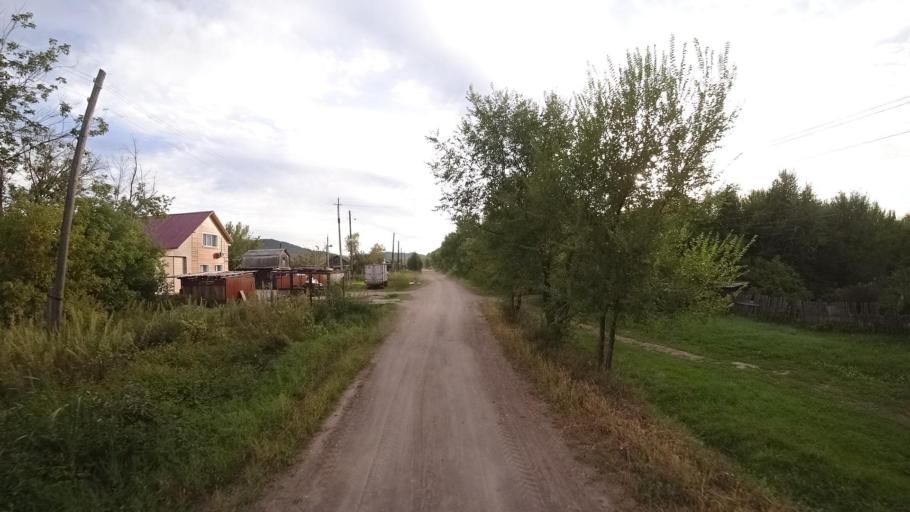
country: RU
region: Primorskiy
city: Yakovlevka
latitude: 44.4218
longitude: 133.4554
